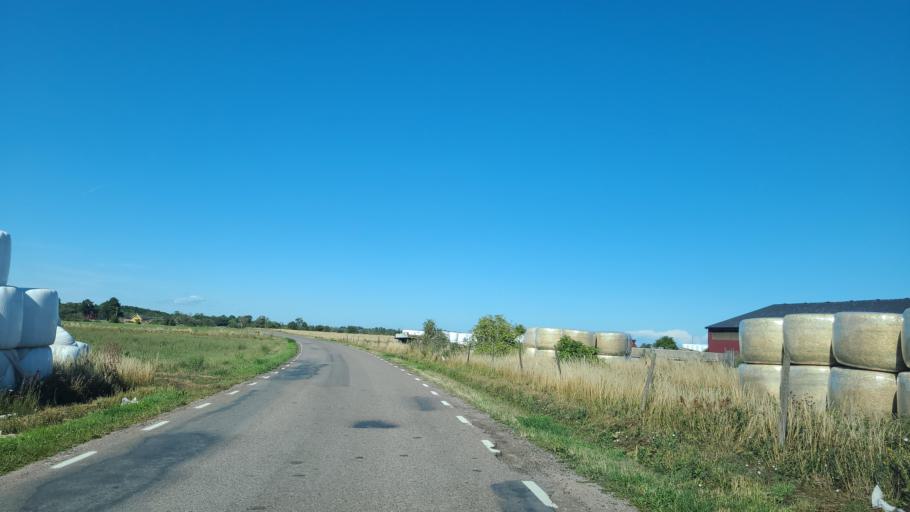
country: SE
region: Kalmar
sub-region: Borgholms Kommun
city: Borgholm
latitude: 56.8607
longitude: 16.8210
